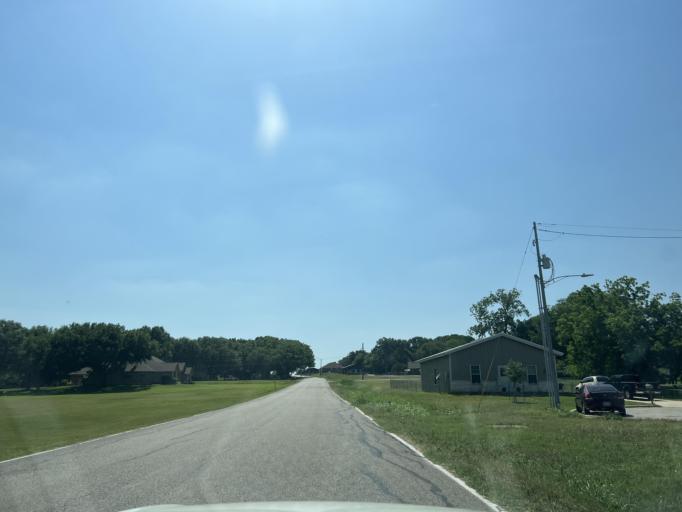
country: US
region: Texas
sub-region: Washington County
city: Brenham
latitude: 30.1621
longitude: -96.4175
